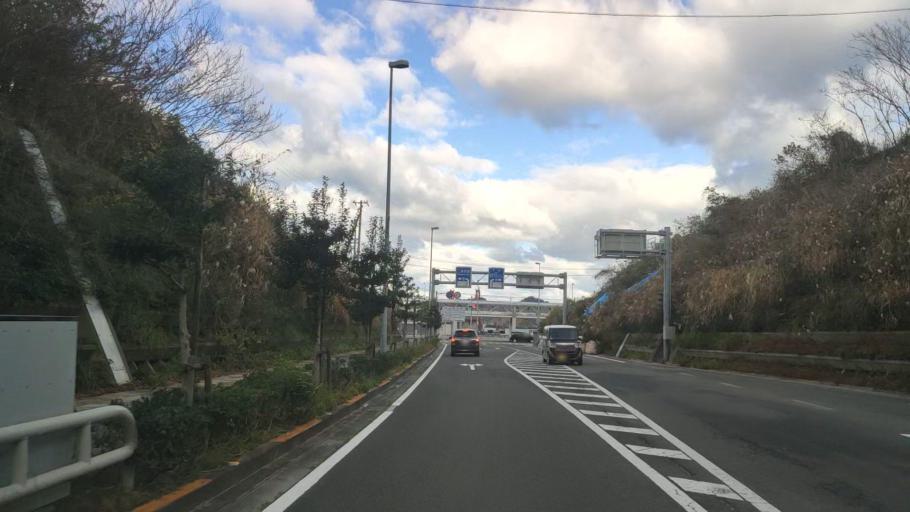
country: JP
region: Ehime
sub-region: Shikoku-chuo Shi
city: Matsuyama
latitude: 33.8881
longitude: 132.7064
